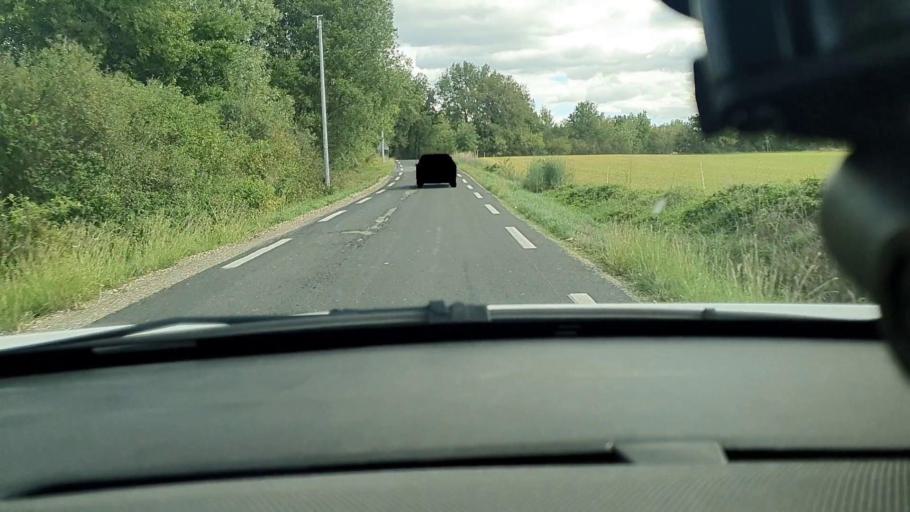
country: FR
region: Languedoc-Roussillon
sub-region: Departement du Gard
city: Les Mages
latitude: 44.1952
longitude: 4.2139
